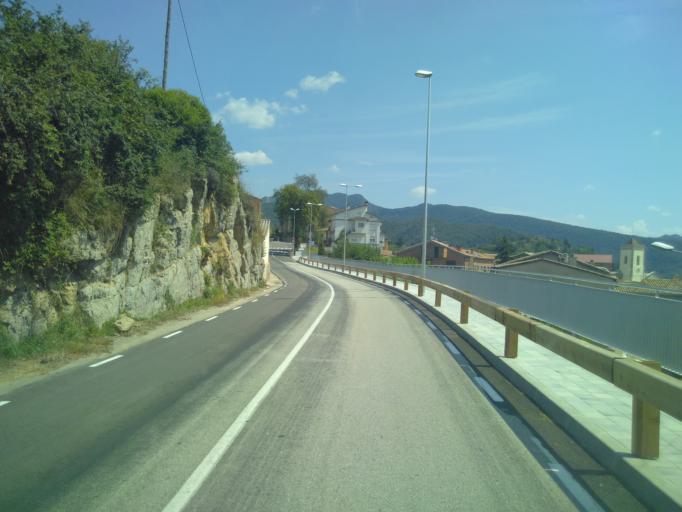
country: ES
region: Catalonia
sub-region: Provincia de Barcelona
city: Montesquiu
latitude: 42.1015
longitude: 2.2209
